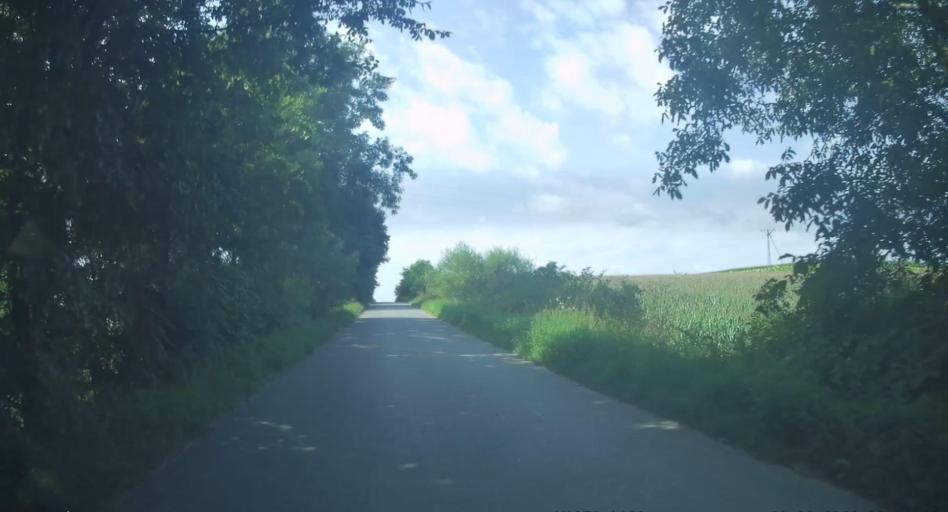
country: PL
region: Lesser Poland Voivodeship
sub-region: Powiat proszowicki
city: Nowe Brzesko
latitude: 50.1497
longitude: 20.4374
